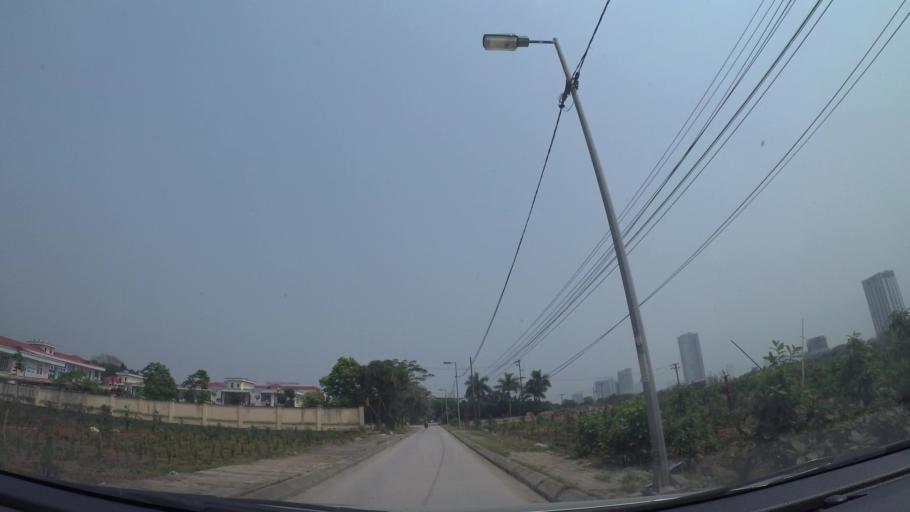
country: VN
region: Ha Noi
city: Ha Dong
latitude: 20.9925
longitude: 105.7679
